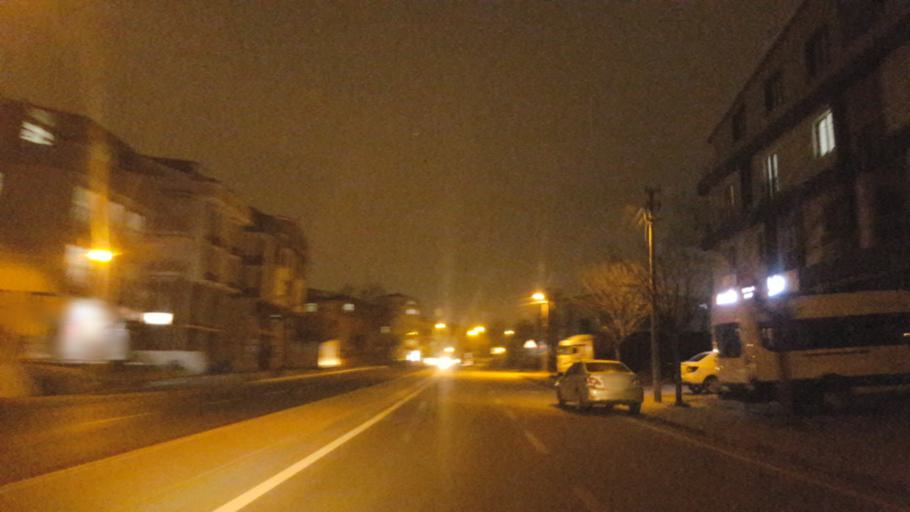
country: TR
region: Kocaeli
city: Darica
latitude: 40.7844
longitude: 29.3994
